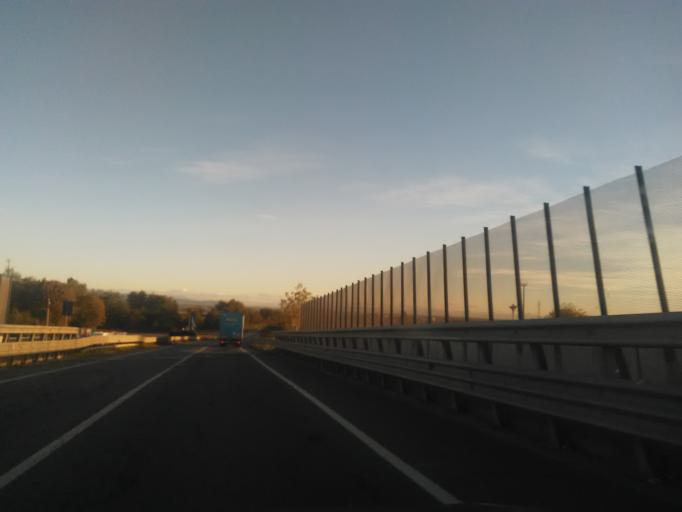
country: IT
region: Piedmont
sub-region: Provincia di Vercelli
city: Carisio
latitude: 45.4362
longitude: 8.2216
